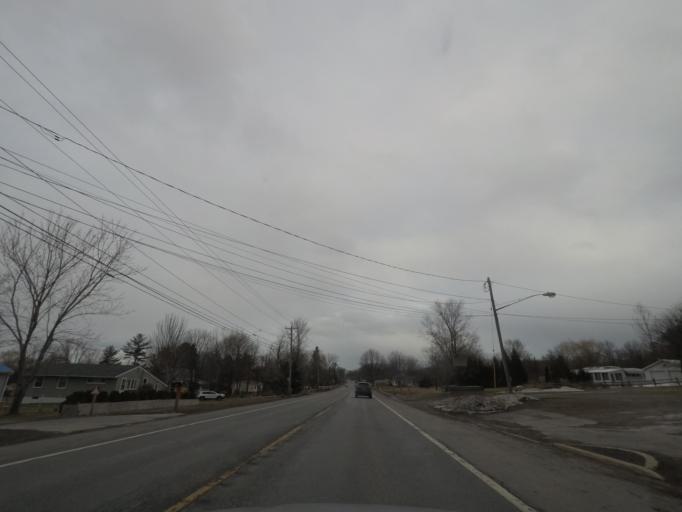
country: US
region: New York
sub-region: Madison County
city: Wampsville
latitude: 43.0743
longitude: -75.7190
